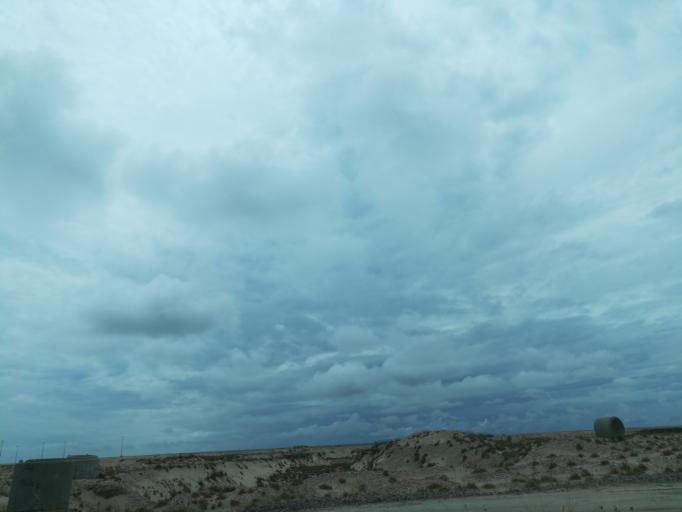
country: NG
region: Lagos
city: Lagos
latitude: 6.4032
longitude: 3.4093
